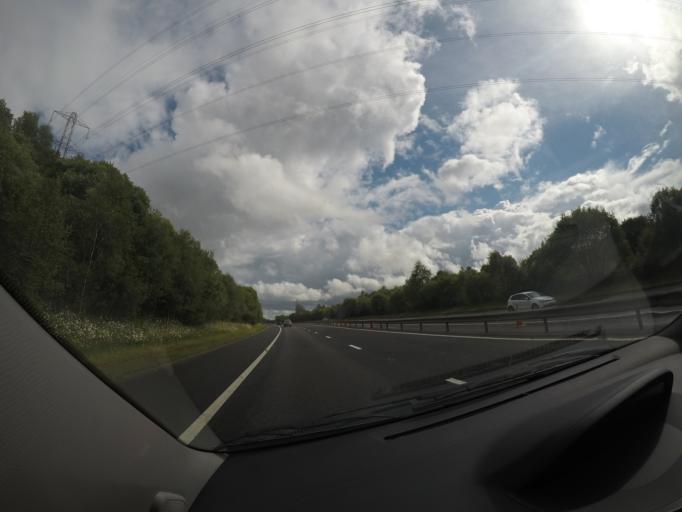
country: GB
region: Scotland
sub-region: North Lanarkshire
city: Chryston
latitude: 55.8808
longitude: -4.0814
